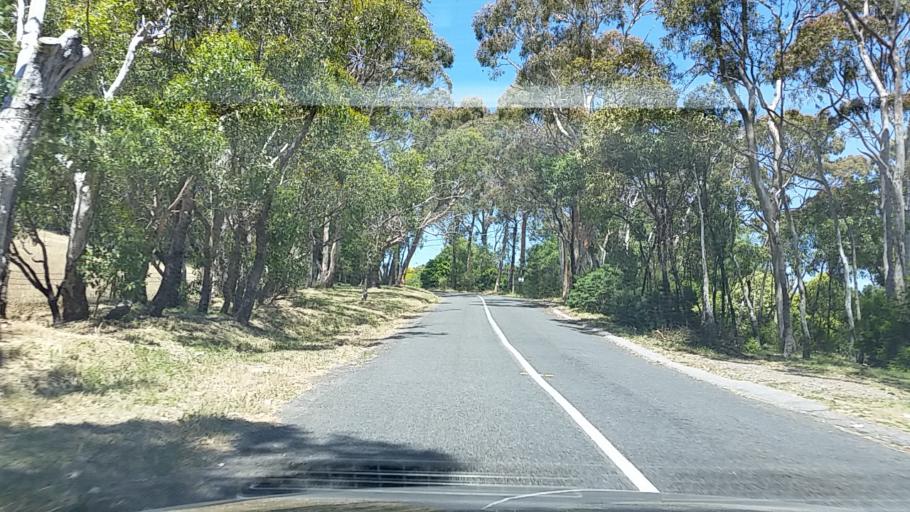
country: AU
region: South Australia
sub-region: Adelaide Hills
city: Upper Sturt
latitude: -35.0011
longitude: 138.6809
